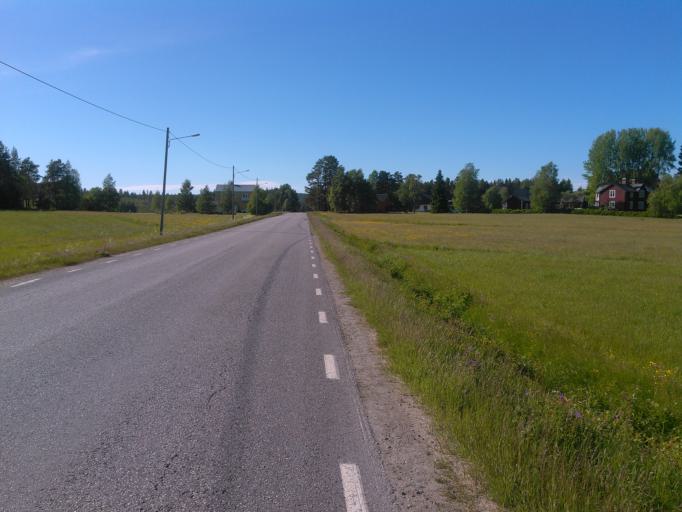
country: SE
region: Vaesterbotten
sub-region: Umea Kommun
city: Roback
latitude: 63.8281
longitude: 20.1174
